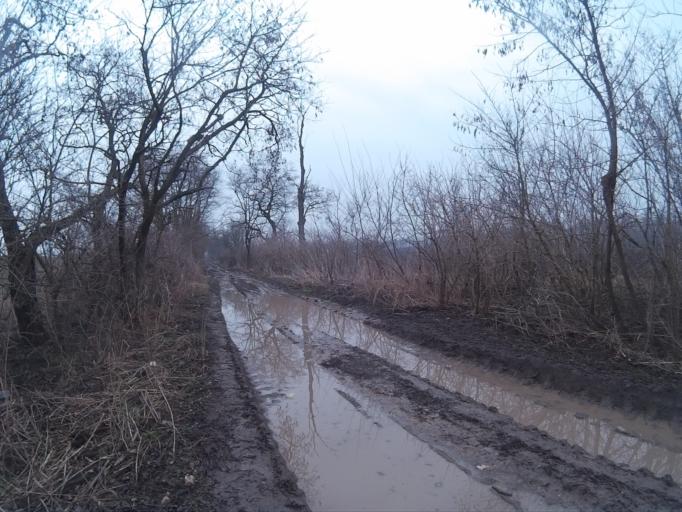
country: HU
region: Fejer
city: Szarliget
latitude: 47.5494
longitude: 18.5643
